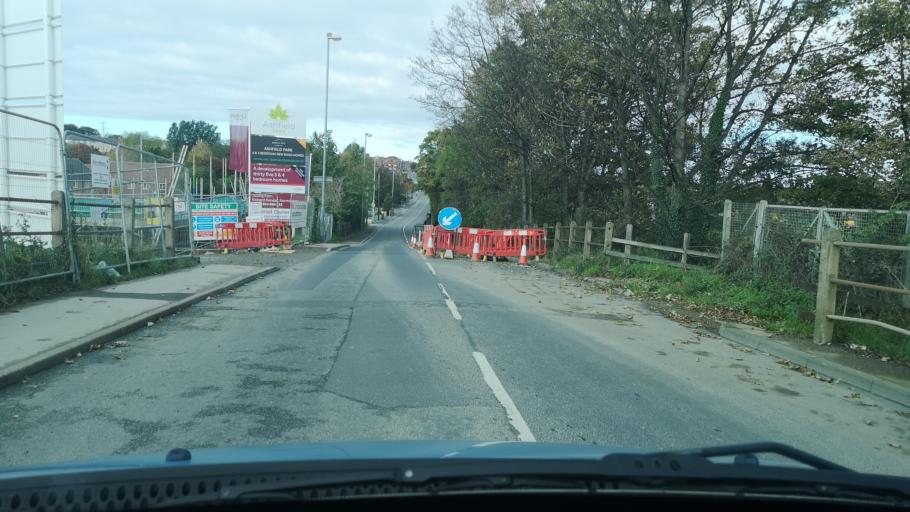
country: GB
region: England
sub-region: City and Borough of Wakefield
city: Normanton
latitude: 53.7024
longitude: -1.4236
